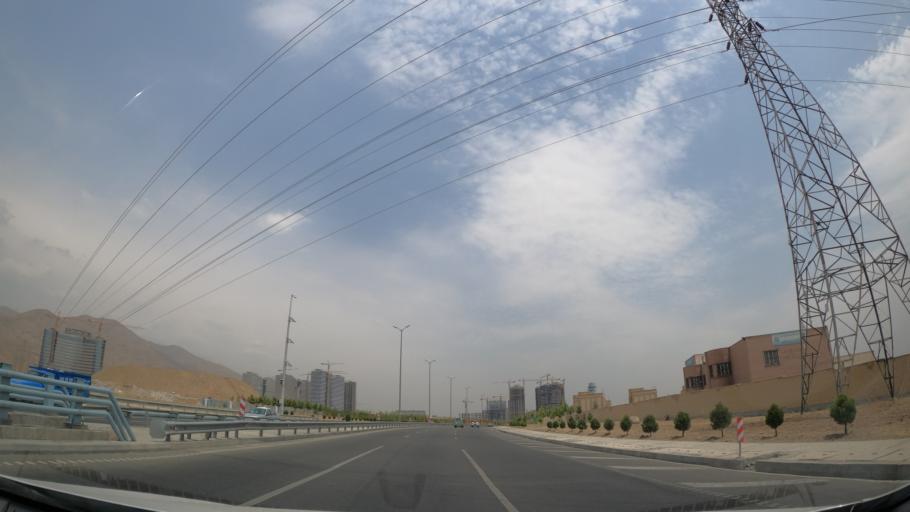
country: IR
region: Tehran
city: Shahr-e Qods
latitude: 35.7515
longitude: 51.1660
